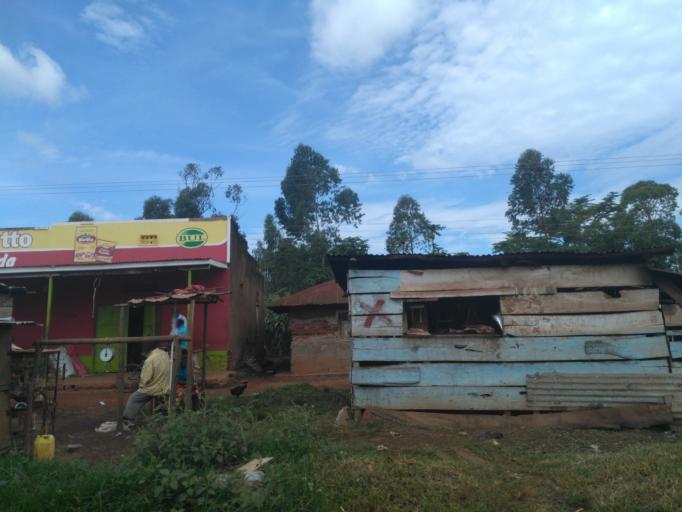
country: UG
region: Central Region
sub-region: Buikwe District
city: Njeru
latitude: 0.3969
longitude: 33.1742
